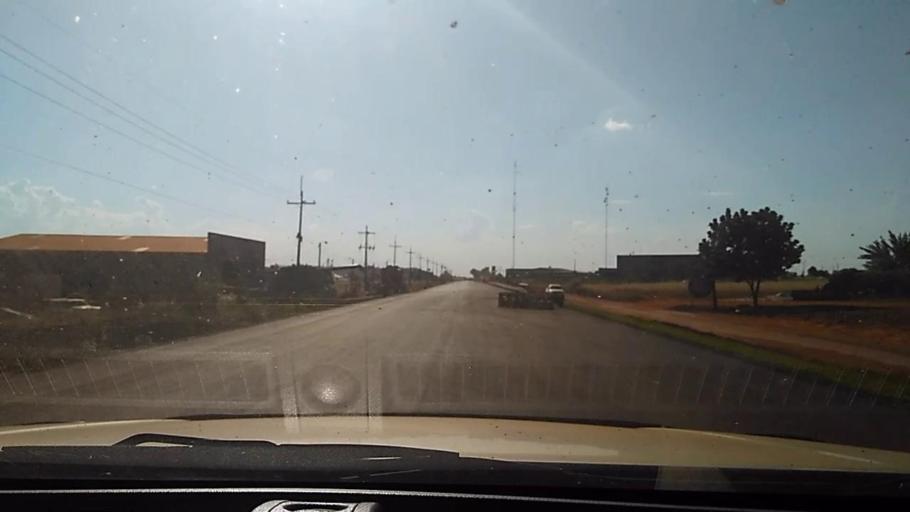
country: PY
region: Alto Parana
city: Naranjal
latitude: -25.9018
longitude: -55.4529
